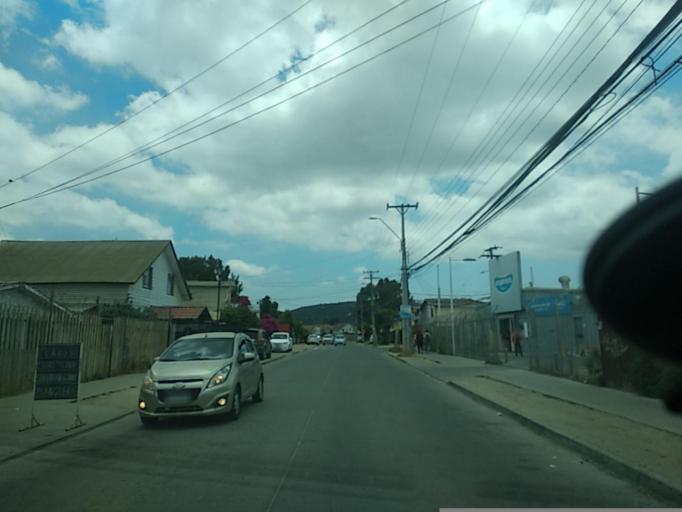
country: CL
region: Valparaiso
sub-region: Provincia de Marga Marga
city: Villa Alemana
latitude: -33.0349
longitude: -71.4056
